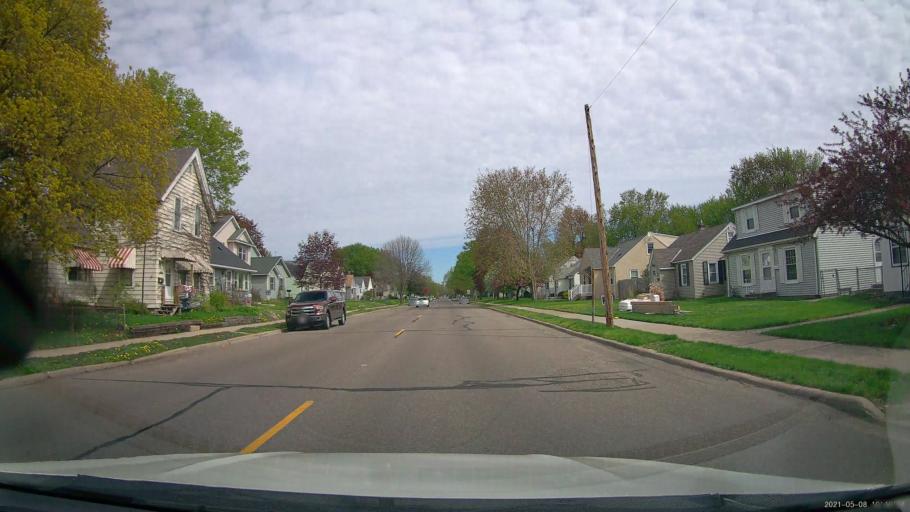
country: US
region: Minnesota
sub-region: Dakota County
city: South Saint Paul
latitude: 44.8966
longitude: -93.0526
